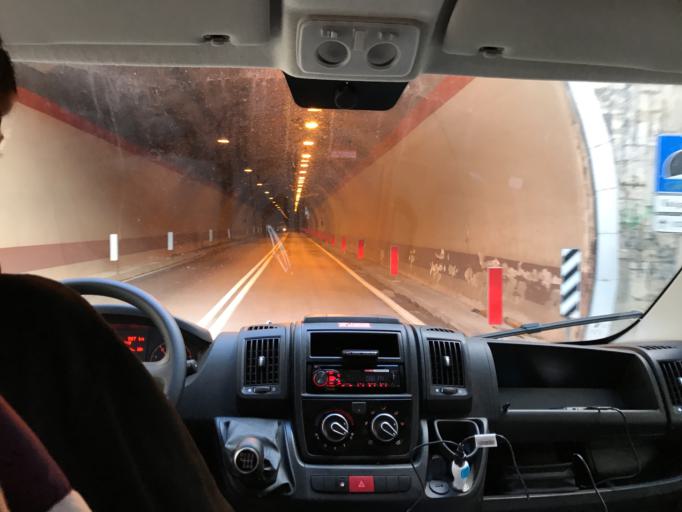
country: IT
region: The Marches
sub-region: Provincia di Ascoli Piceno
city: Arquata del Tronto
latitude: 42.7643
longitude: 13.3423
